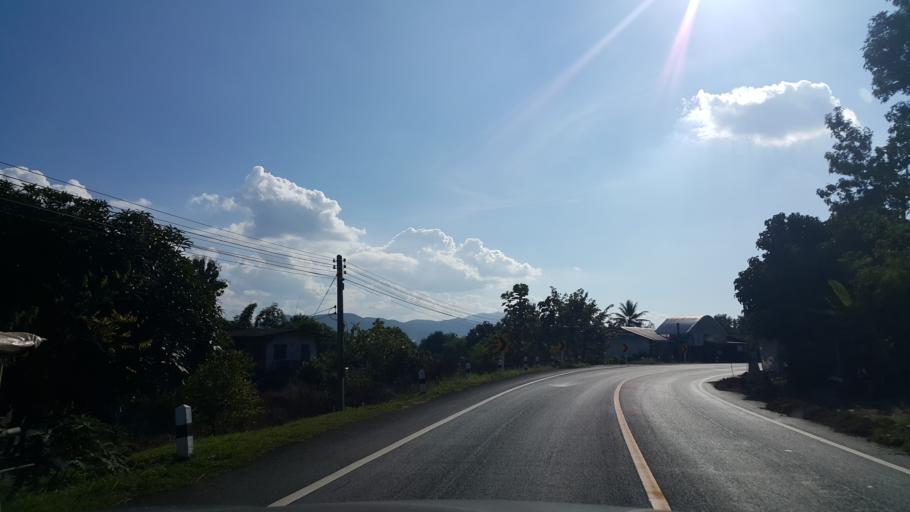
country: TH
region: Lamphun
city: Mae Tha
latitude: 18.4738
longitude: 99.1633
